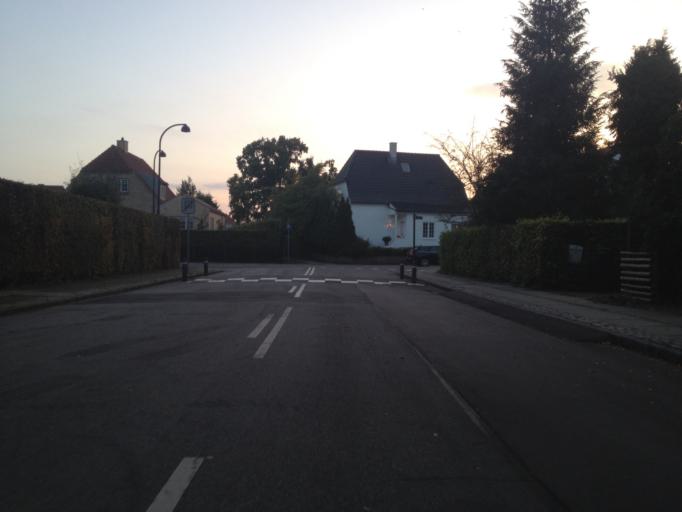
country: DK
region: Capital Region
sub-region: Gentofte Kommune
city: Charlottenlund
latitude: 55.7510
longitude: 12.5630
